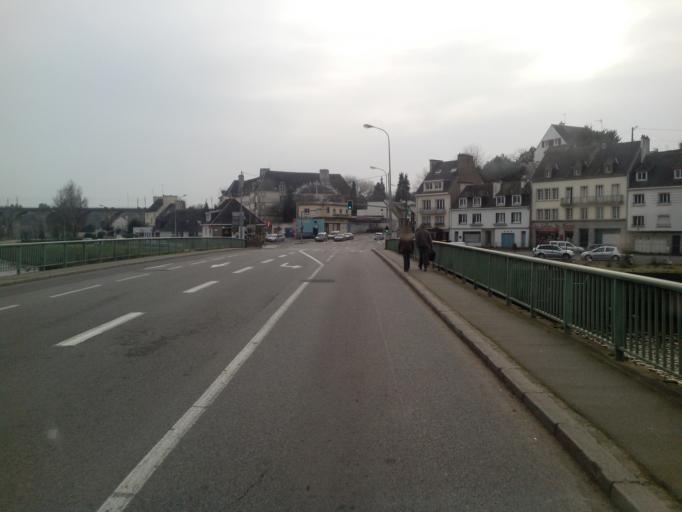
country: FR
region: Brittany
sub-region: Departement du Morbihan
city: Hennebont
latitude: 47.8031
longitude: -3.2788
